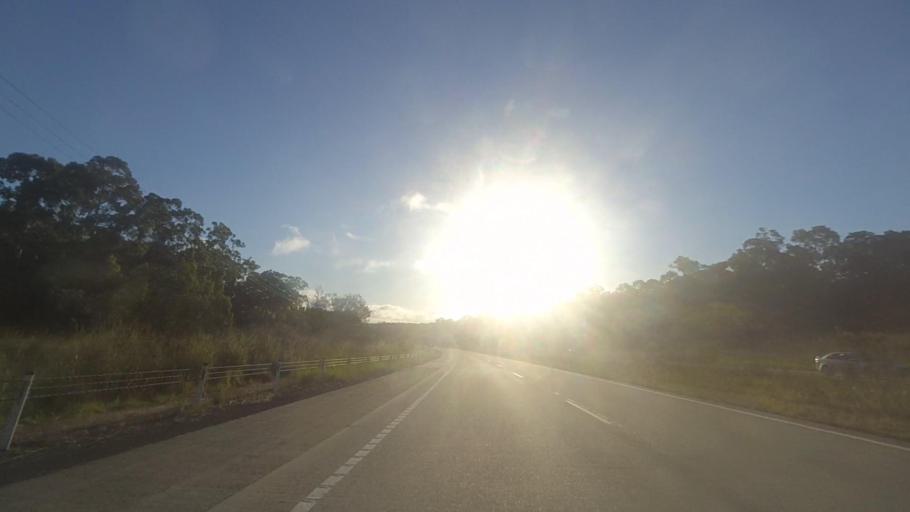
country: AU
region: New South Wales
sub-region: Great Lakes
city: Hawks Nest
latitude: -32.5373
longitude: 152.1725
